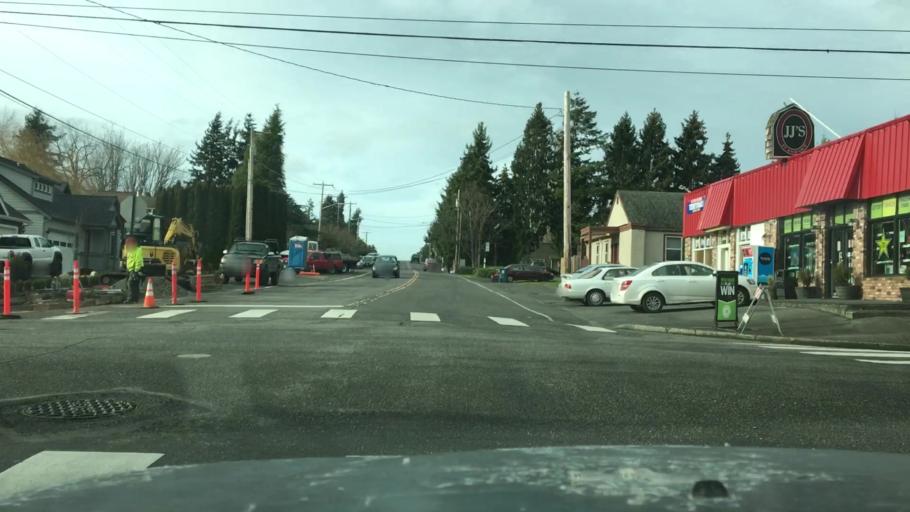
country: US
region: Washington
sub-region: Whatcom County
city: Bellingham
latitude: 48.7202
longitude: -122.4902
